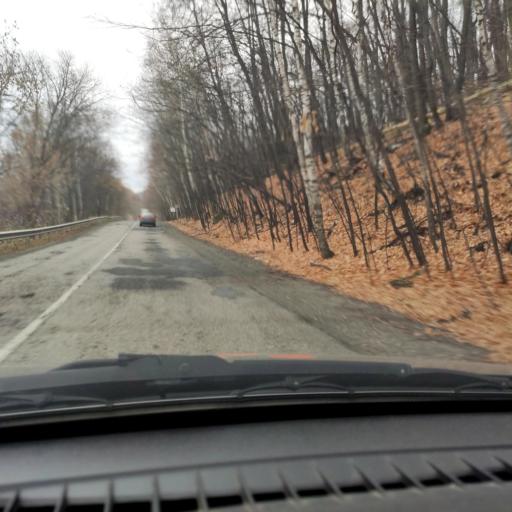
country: RU
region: Samara
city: Pribrezhnyy
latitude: 53.4379
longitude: 49.7201
